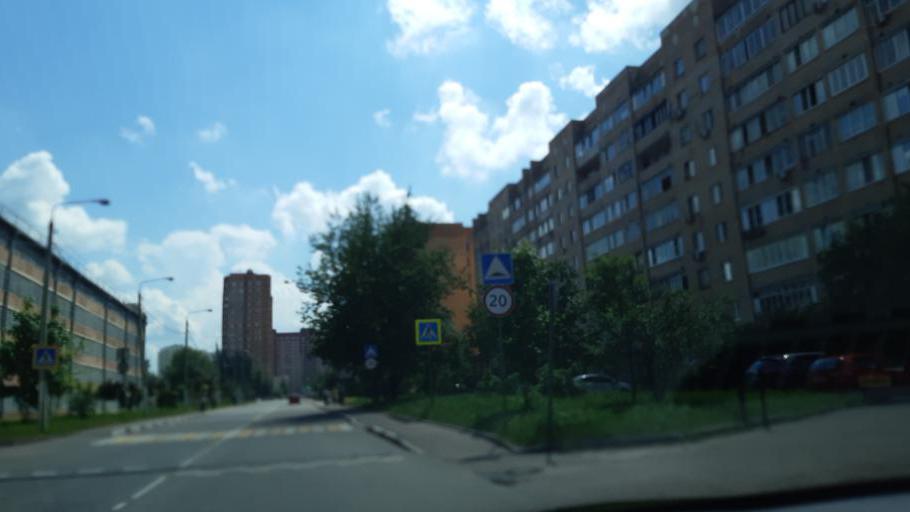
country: RU
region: Moskovskaya
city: Dolgoprudnyy
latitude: 55.9404
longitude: 37.4985
